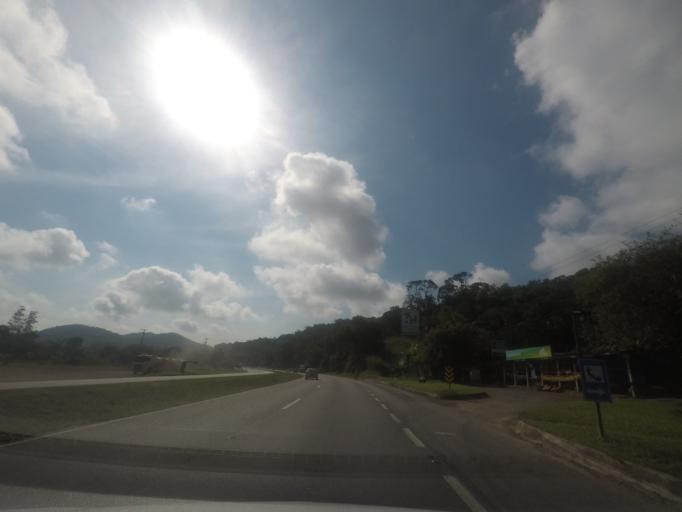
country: BR
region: Parana
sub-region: Antonina
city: Antonina
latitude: -25.5449
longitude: -48.7808
